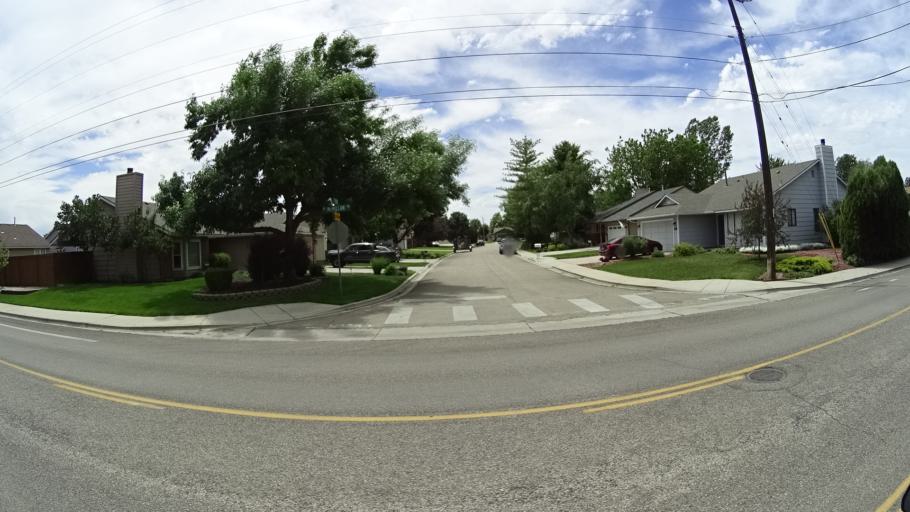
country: US
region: Idaho
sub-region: Ada County
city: Eagle
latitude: 43.6485
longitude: -116.3203
